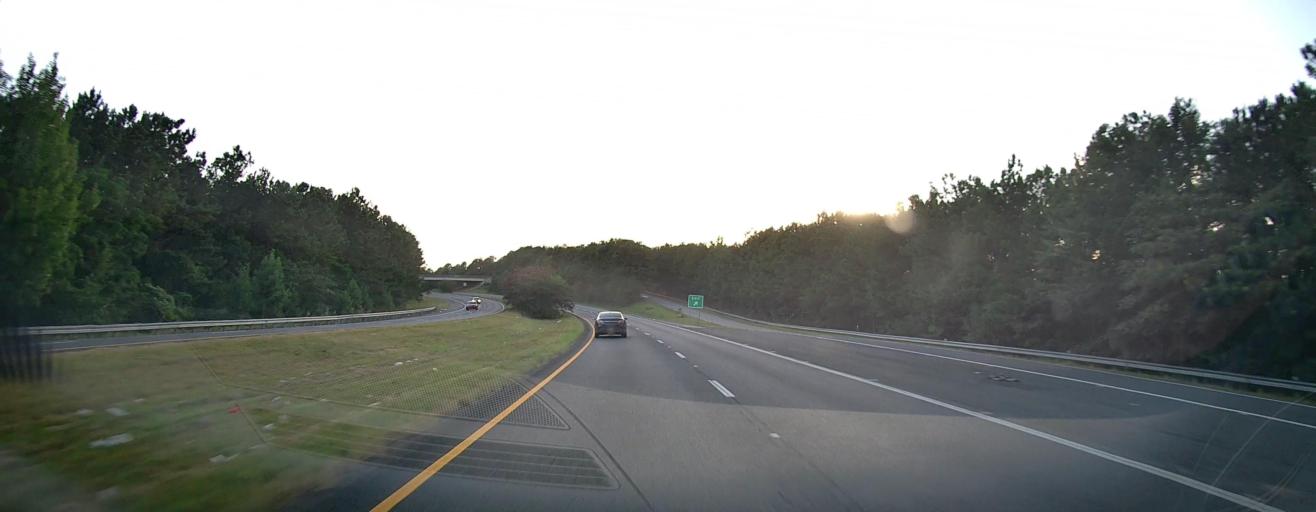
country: US
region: Georgia
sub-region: Muscogee County
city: Columbus
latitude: 32.5202
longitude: -84.9108
